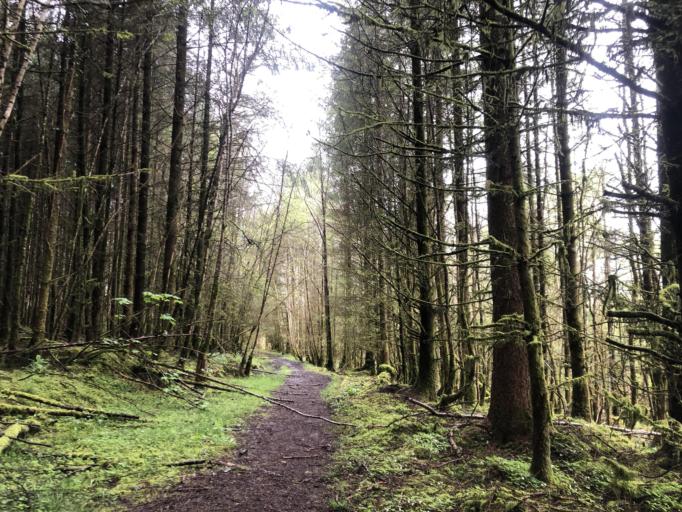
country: IE
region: Connaught
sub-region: County Leitrim
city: Carrick-on-Shannon
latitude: 53.9869
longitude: -8.1776
